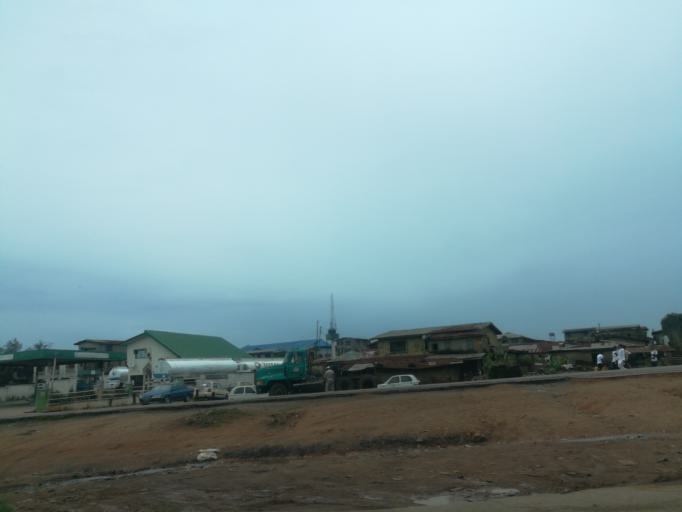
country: NG
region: Oyo
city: Ibadan
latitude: 7.3608
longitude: 3.9252
